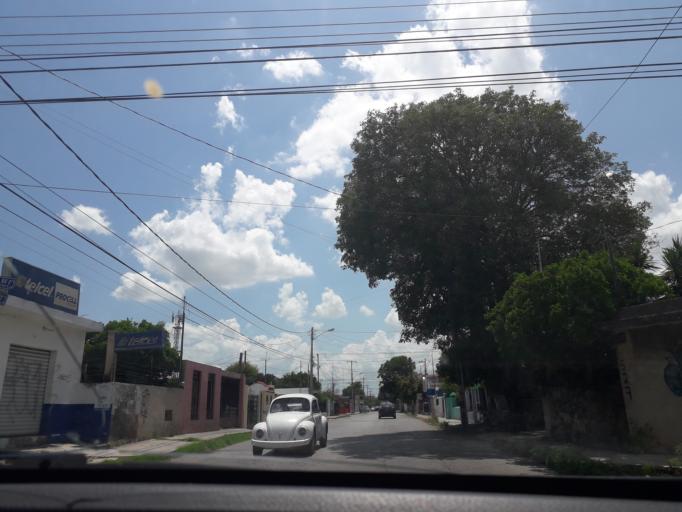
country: MX
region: Yucatan
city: Merida
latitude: 20.9644
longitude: -89.6464
